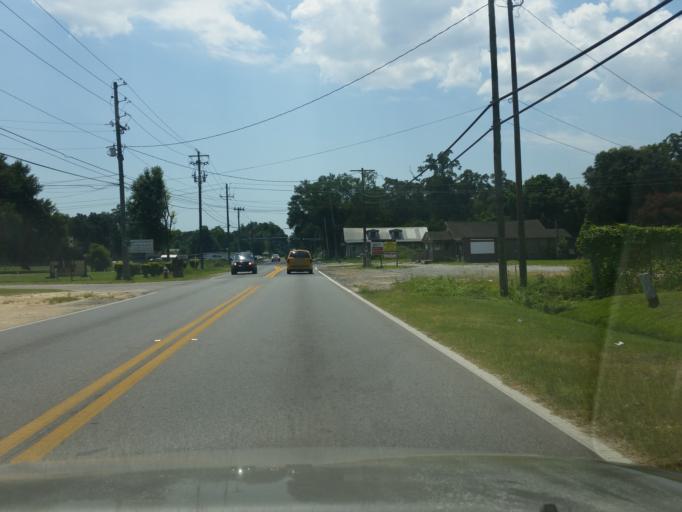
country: US
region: Florida
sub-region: Escambia County
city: Ensley
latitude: 30.5208
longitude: -87.2674
